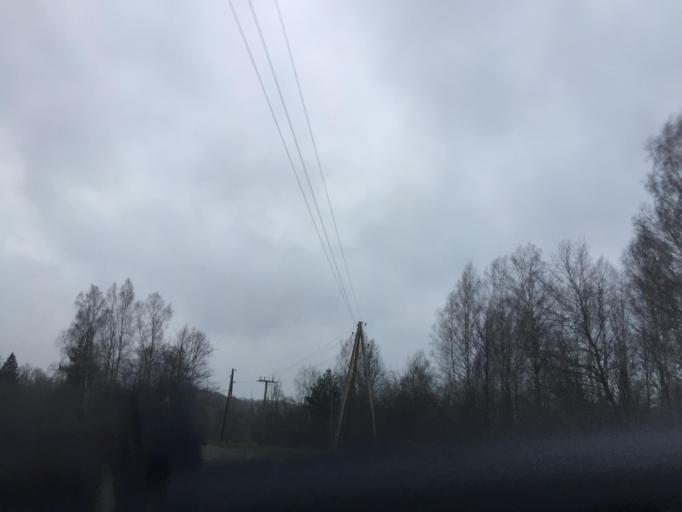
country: LV
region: Salacgrivas
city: Salacgriva
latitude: 57.7607
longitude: 24.4551
